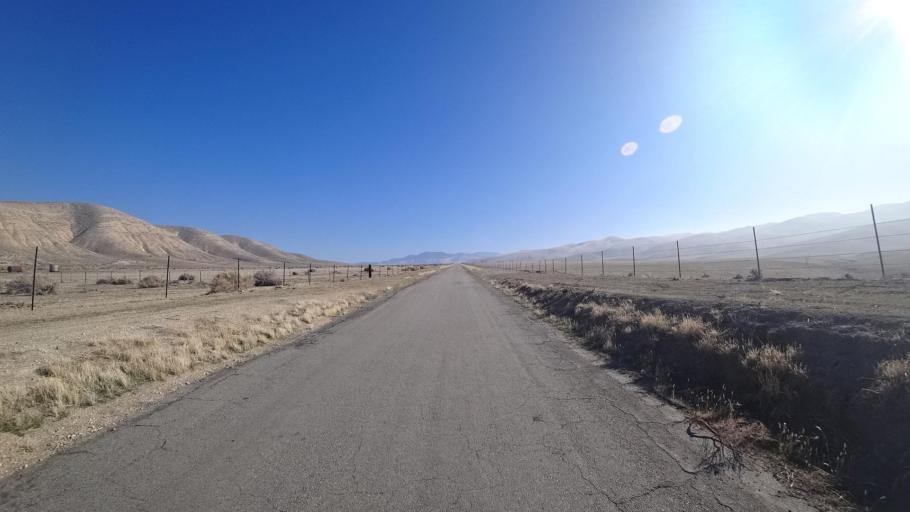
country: US
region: California
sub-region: Kern County
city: Maricopa
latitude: 35.0038
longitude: -119.4069
